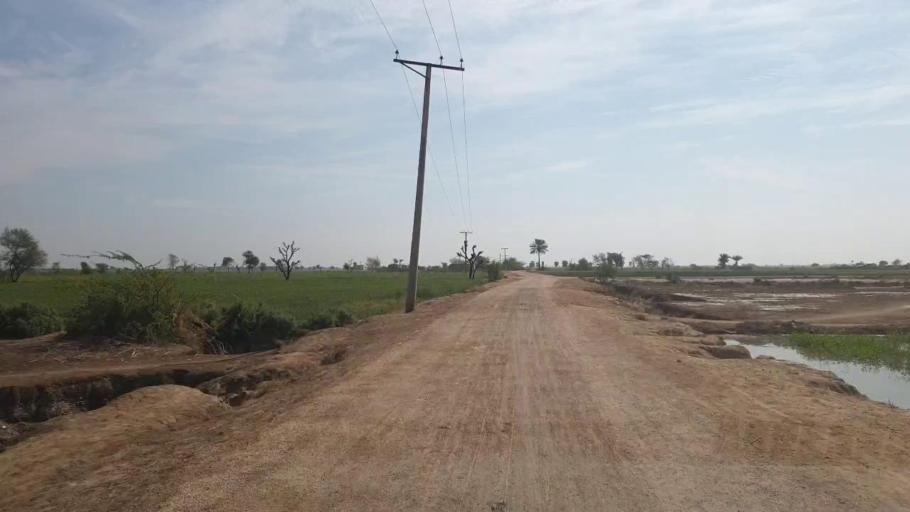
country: PK
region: Sindh
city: Samaro
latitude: 25.3628
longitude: 69.2623
